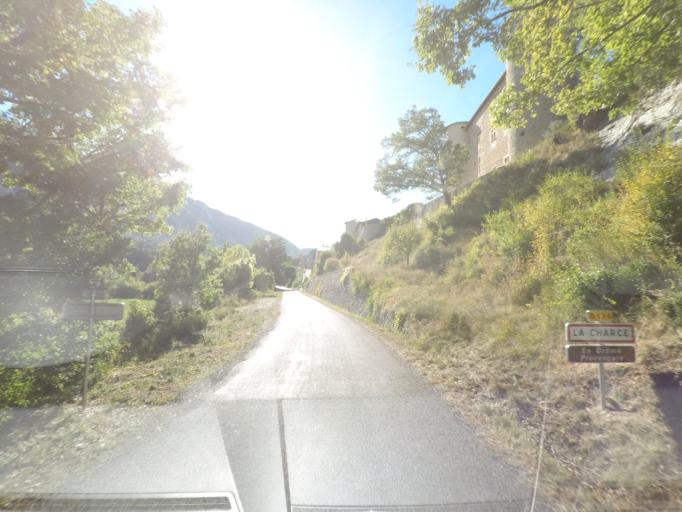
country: FR
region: Provence-Alpes-Cote d'Azur
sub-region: Departement des Hautes-Alpes
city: Serres
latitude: 44.4709
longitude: 5.4529
